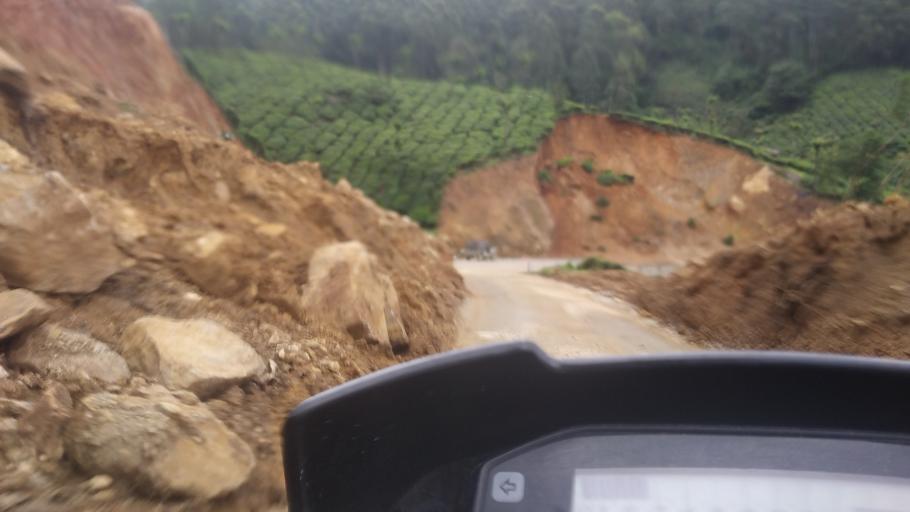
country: IN
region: Kerala
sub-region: Idukki
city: Munnar
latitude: 10.0369
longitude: 77.1518
